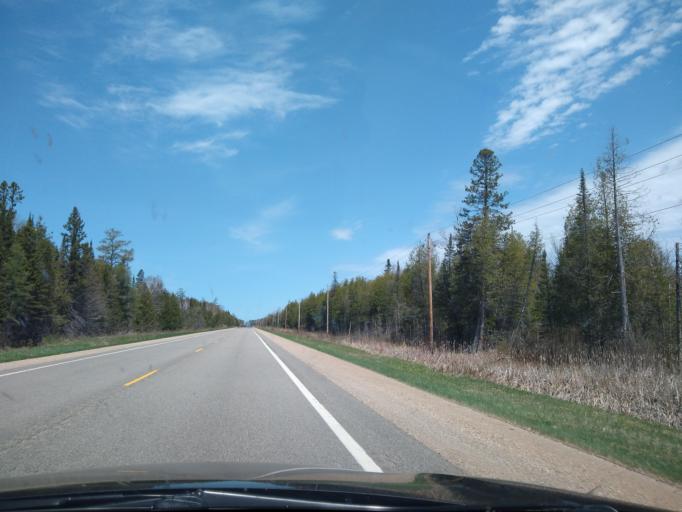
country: US
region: Michigan
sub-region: Delta County
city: Gladstone
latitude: 46.1040
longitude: -86.9807
